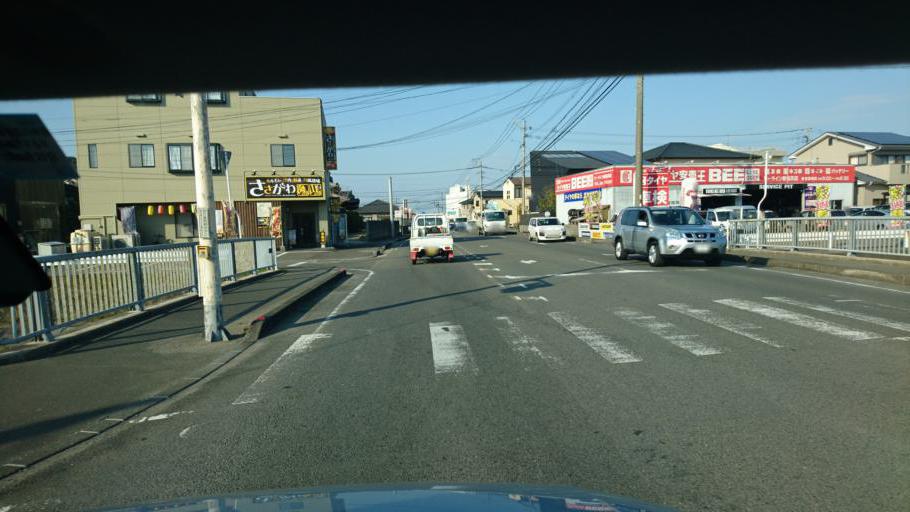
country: JP
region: Miyazaki
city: Miyazaki-shi
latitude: 31.9757
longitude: 131.4402
